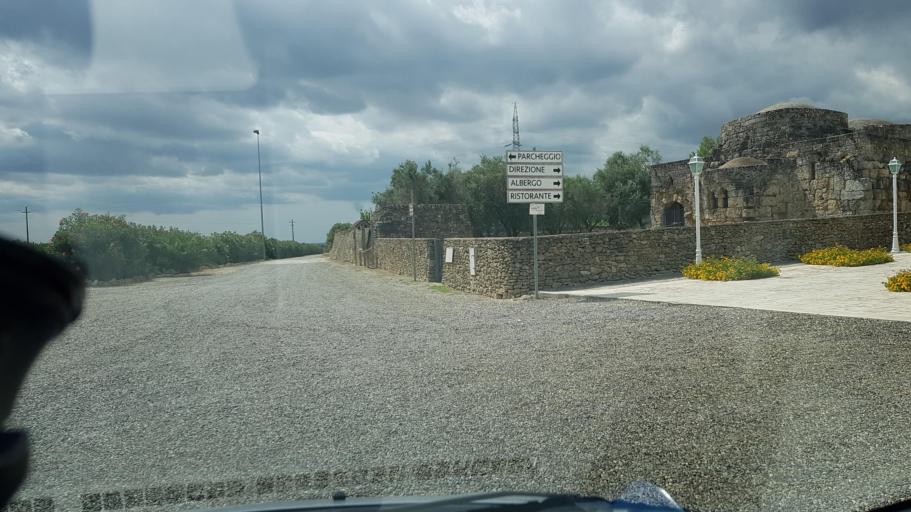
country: IT
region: Apulia
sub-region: Provincia di Brindisi
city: Torre Santa Susanna
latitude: 40.5007
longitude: 17.7637
